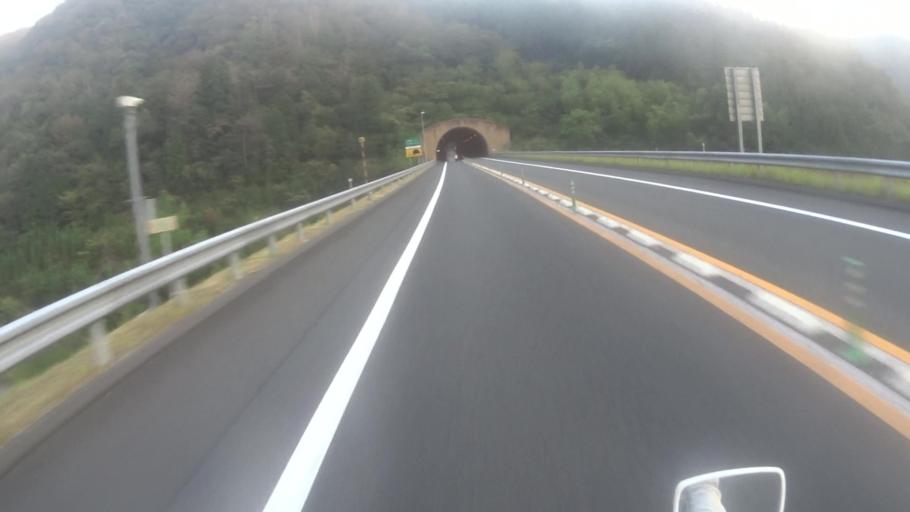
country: JP
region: Kyoto
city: Miyazu
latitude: 35.4625
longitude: 135.1739
